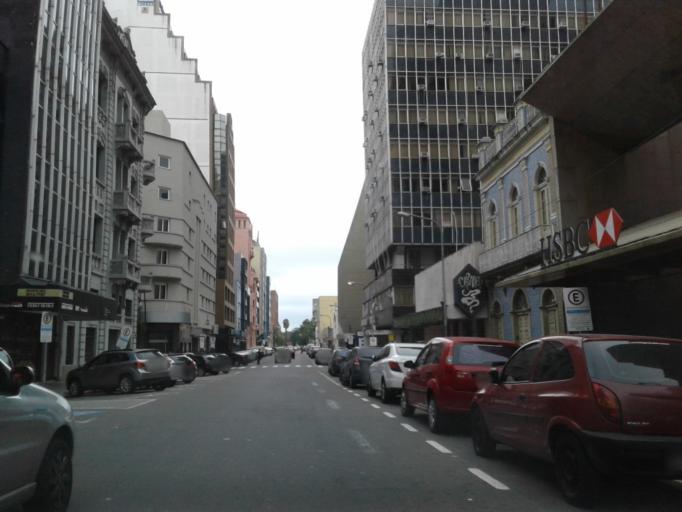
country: BR
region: Rio Grande do Sul
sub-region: Porto Alegre
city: Porto Alegre
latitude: -30.0302
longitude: -51.2332
